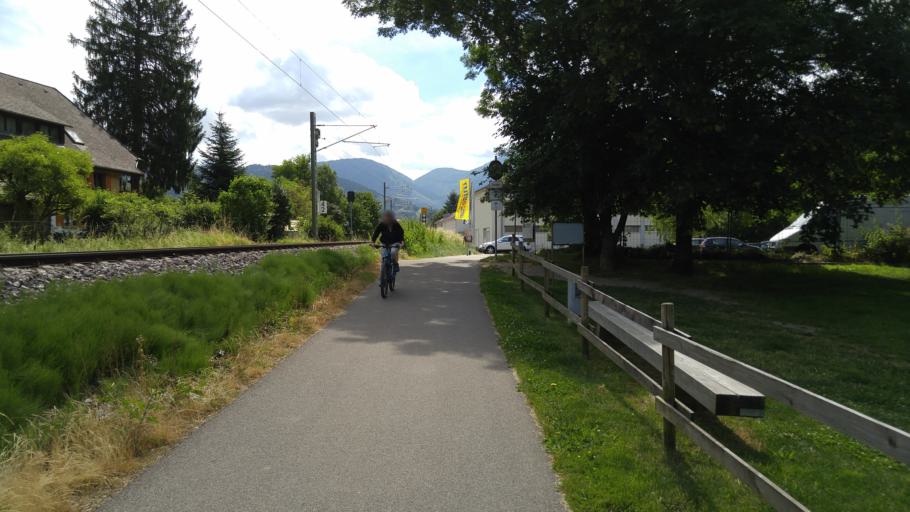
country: DE
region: Baden-Wuerttemberg
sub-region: Freiburg Region
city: Muenstertal/Schwarzwald
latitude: 47.8602
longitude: 7.7609
